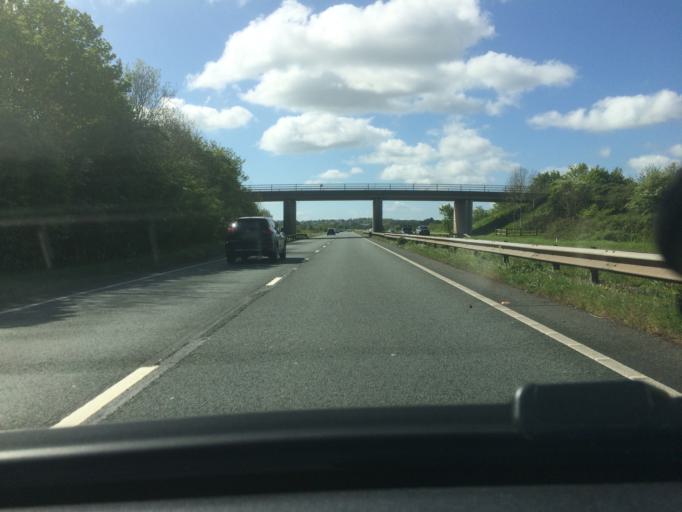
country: GB
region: Wales
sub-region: Wrexham
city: Rossett
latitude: 53.1219
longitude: -2.9498
